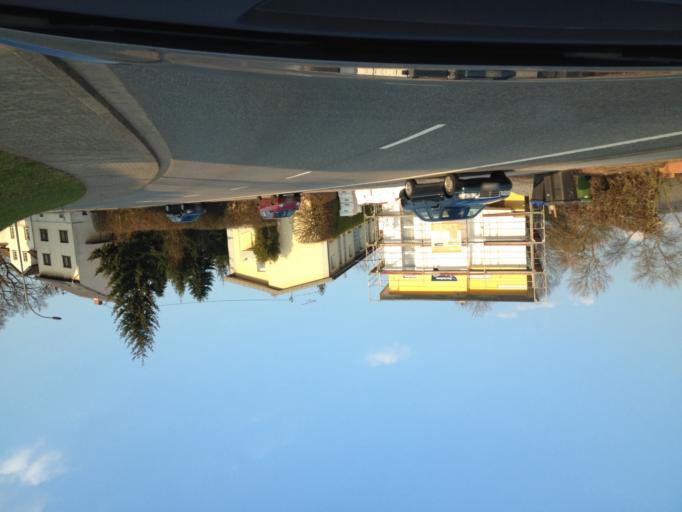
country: DE
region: Saarland
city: Sankt Wendel
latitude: 49.4645
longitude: 7.1762
